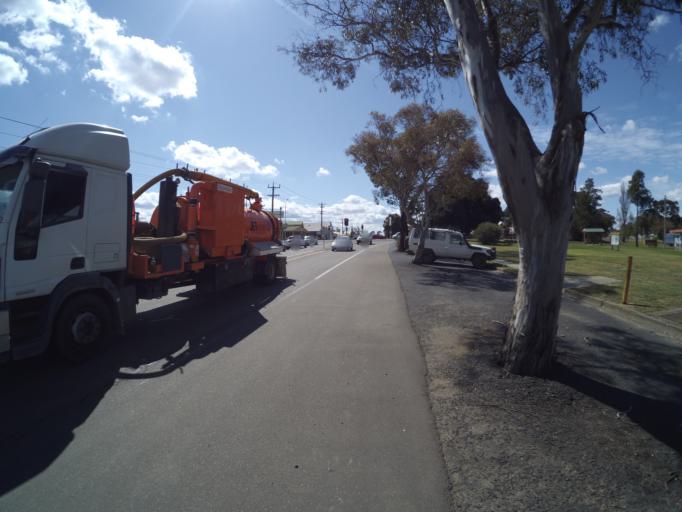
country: AU
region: New South Wales
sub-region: Goulburn Mulwaree
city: Goulburn
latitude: -34.7462
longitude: 149.7333
